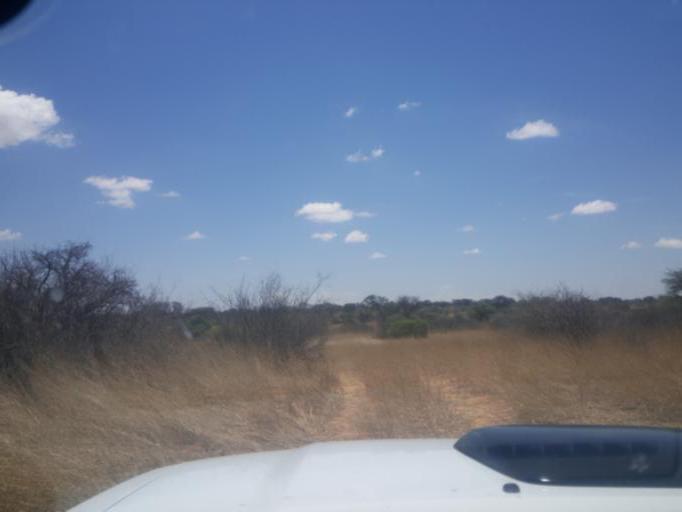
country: BW
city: Lokwabe
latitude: -24.9255
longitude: 21.4504
